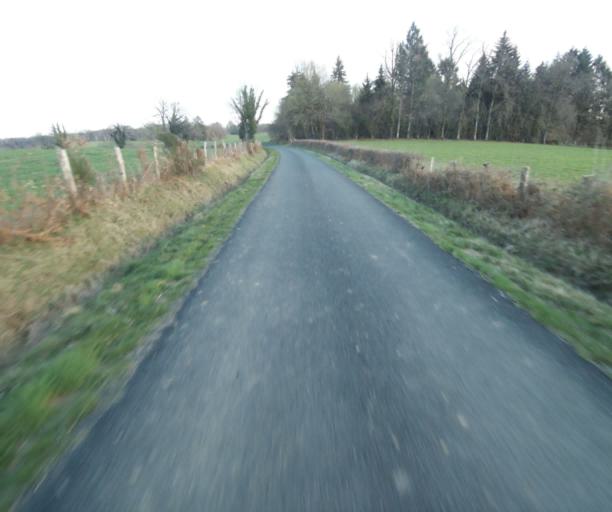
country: FR
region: Limousin
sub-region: Departement de la Correze
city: Uzerche
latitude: 45.3690
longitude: 1.5957
